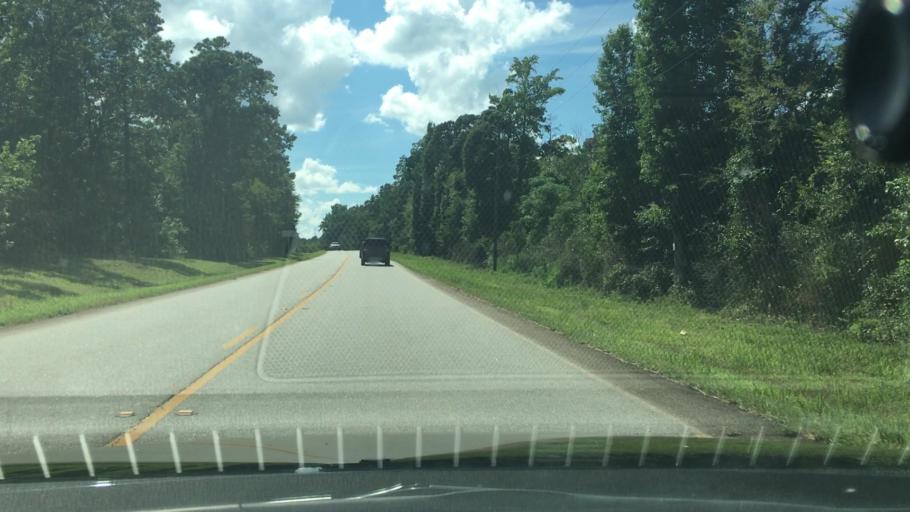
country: US
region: Georgia
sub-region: Jasper County
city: Monticello
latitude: 33.3055
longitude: -83.6065
